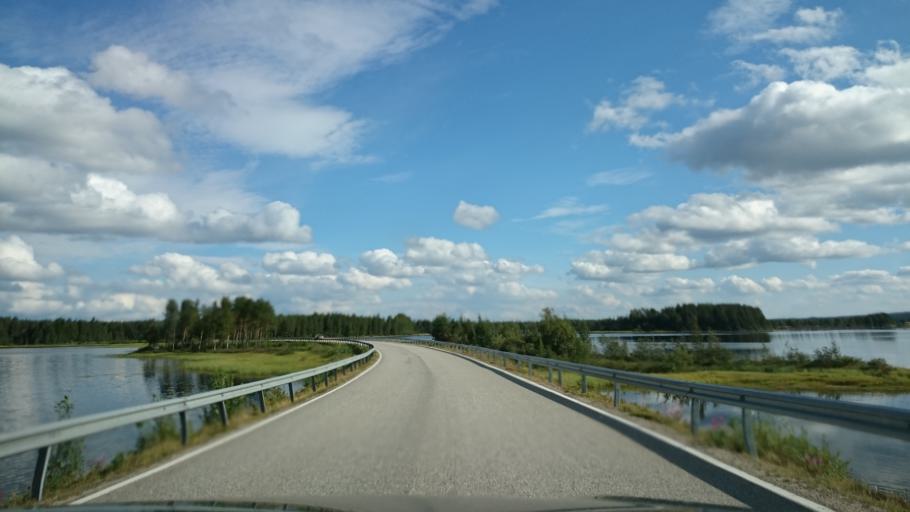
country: FI
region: Kainuu
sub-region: Kehys-Kainuu
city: Suomussalmi
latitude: 64.7626
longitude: 29.3740
